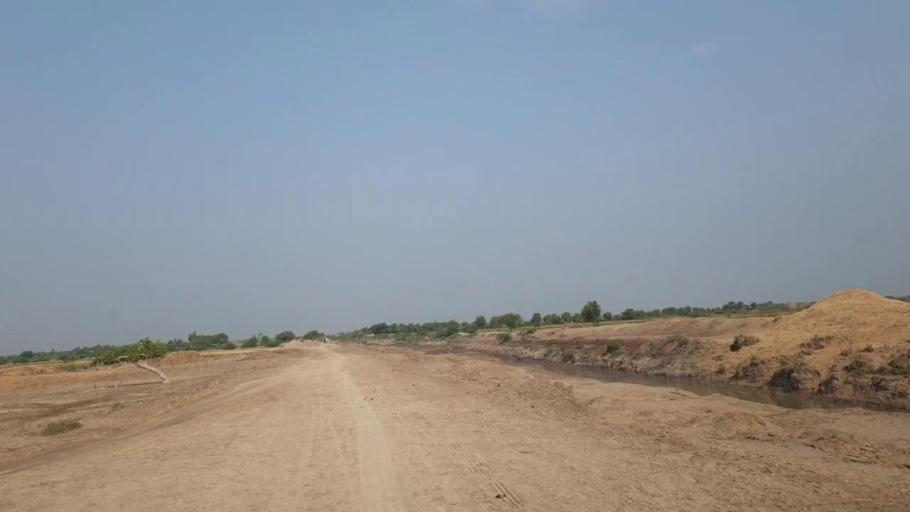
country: PK
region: Sindh
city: Badin
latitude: 24.7301
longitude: 68.7677
